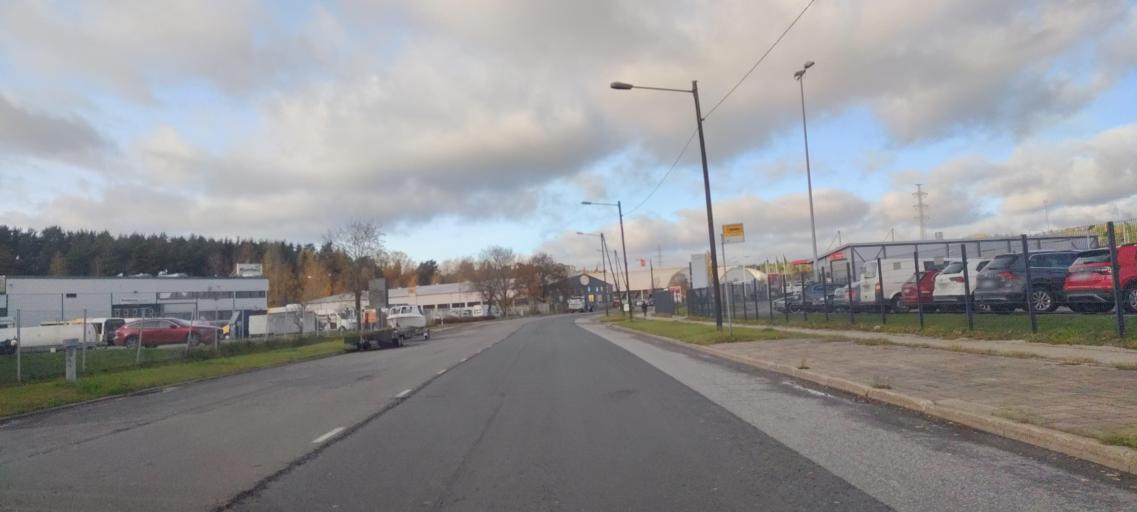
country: FI
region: Varsinais-Suomi
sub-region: Turku
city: Turku
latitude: 60.4750
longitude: 22.2577
